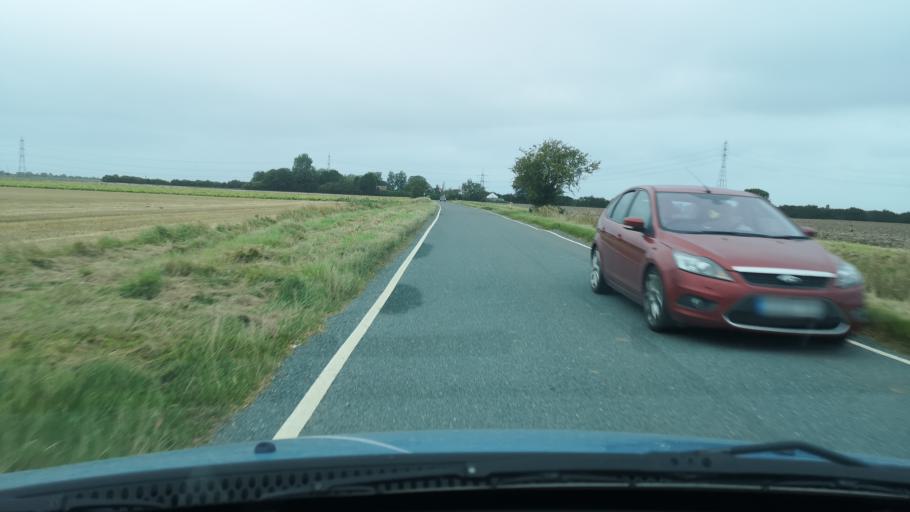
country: GB
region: England
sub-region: North Lincolnshire
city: Burton upon Stather
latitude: 53.6975
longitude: -0.7307
